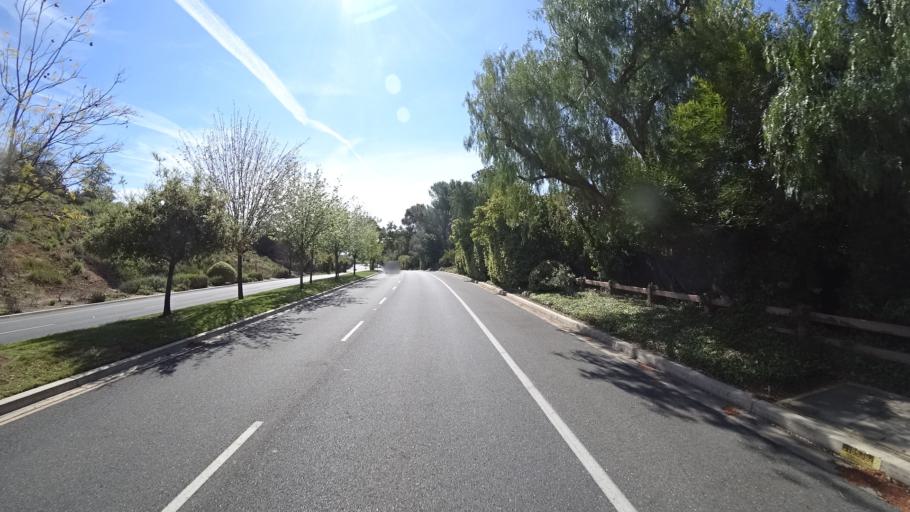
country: US
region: California
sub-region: Ventura County
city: Oak Park
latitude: 34.1936
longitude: -118.8014
